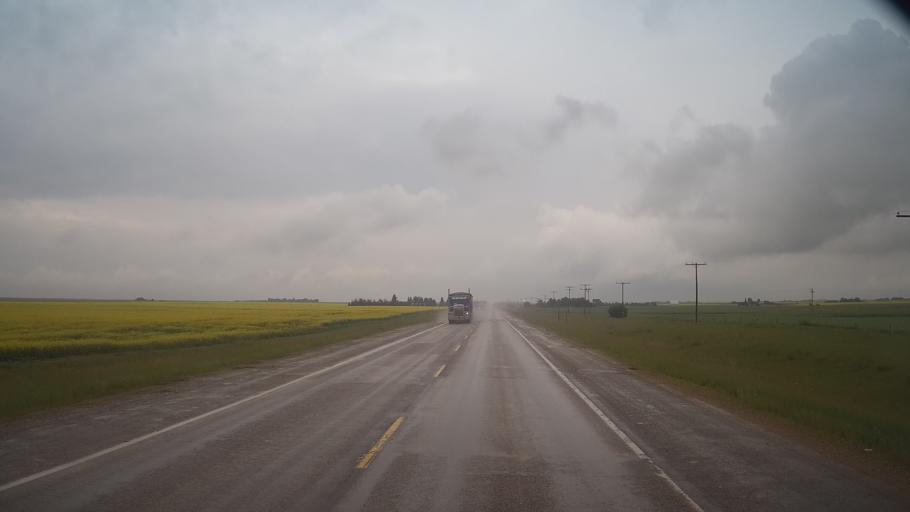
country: CA
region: Saskatchewan
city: Unity
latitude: 52.4349
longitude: -109.0211
